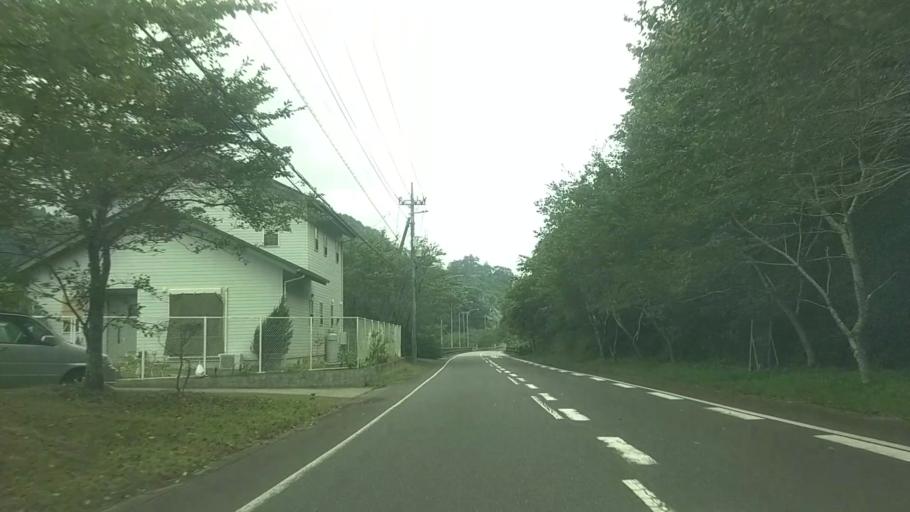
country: JP
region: Chiba
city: Kimitsu
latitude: 35.2316
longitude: 139.9666
